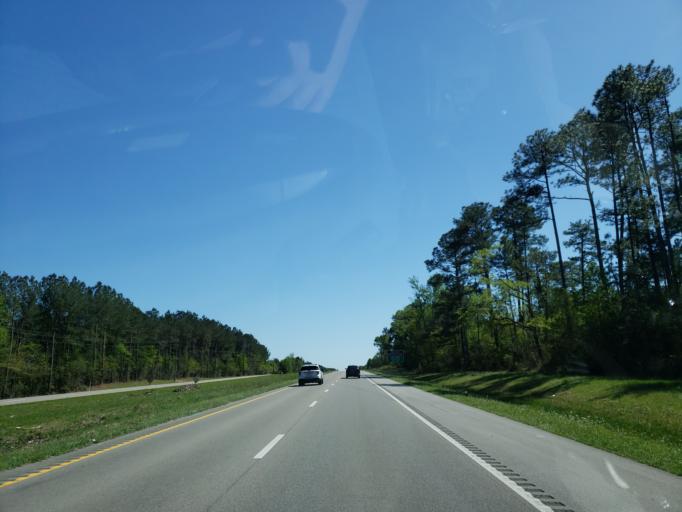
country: US
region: Mississippi
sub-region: Stone County
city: Wiggins
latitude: 31.0273
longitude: -89.2024
